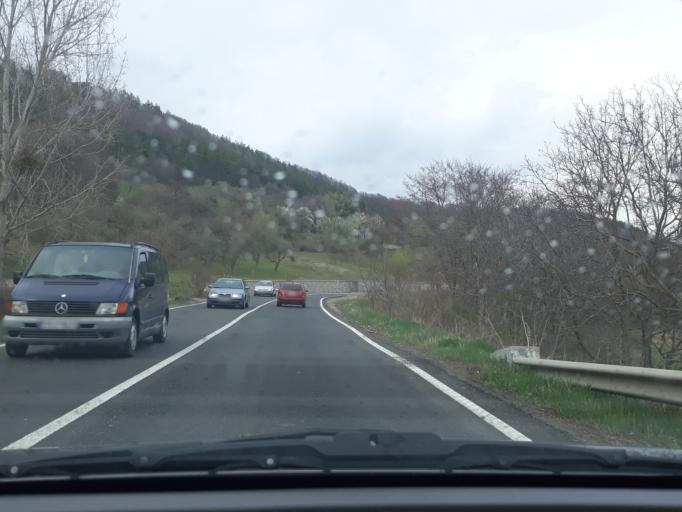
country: RO
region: Harghita
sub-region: Comuna Lupeni
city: Lupeni
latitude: 46.4104
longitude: 25.2189
